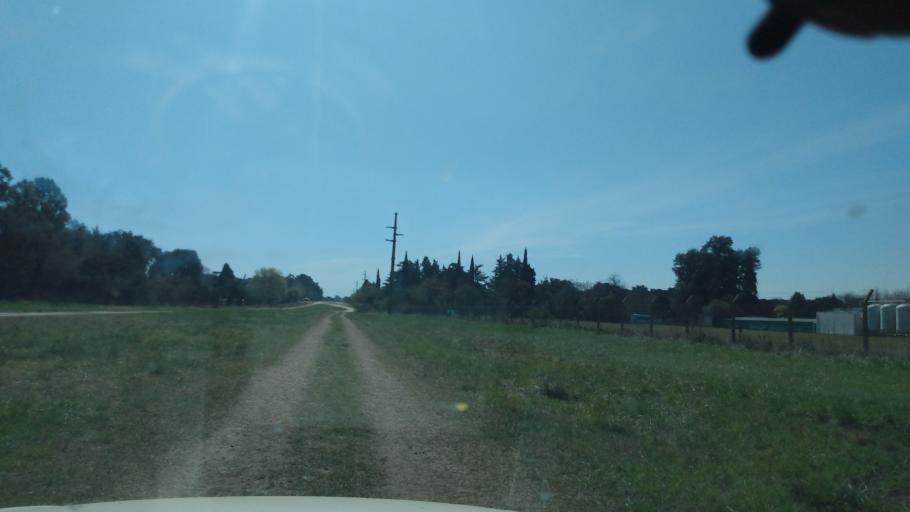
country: AR
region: Buenos Aires
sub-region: Partido de Lujan
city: Lujan
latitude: -34.5757
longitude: -59.1328
